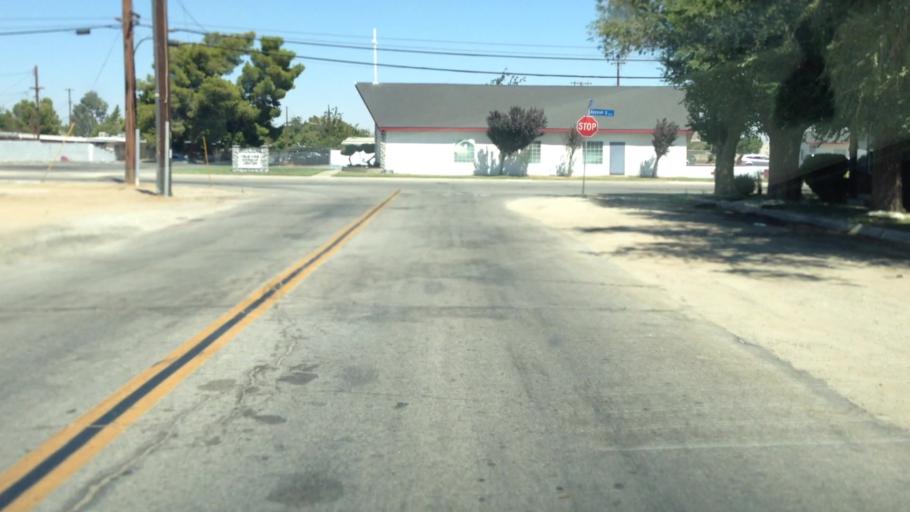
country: US
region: California
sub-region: Los Angeles County
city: Palmdale
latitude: 34.5868
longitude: -118.1144
